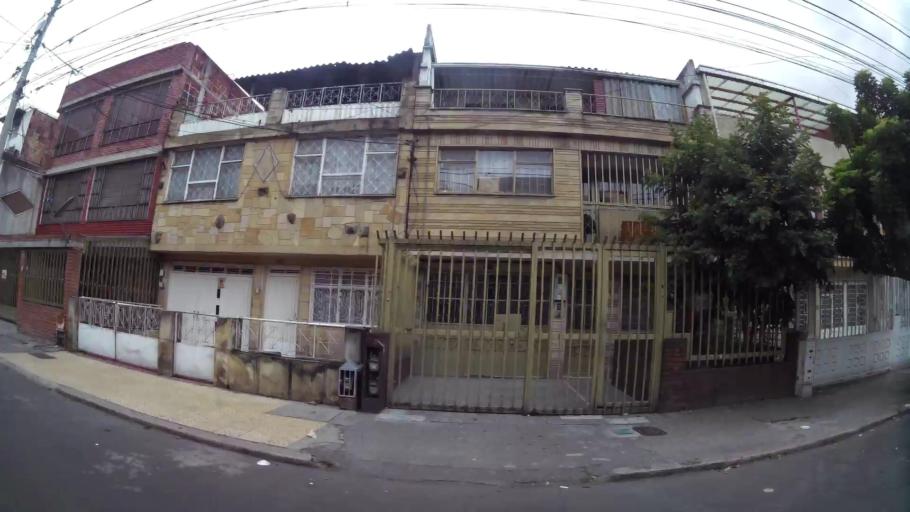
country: CO
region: Bogota D.C.
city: Bogota
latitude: 4.6208
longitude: -74.1170
